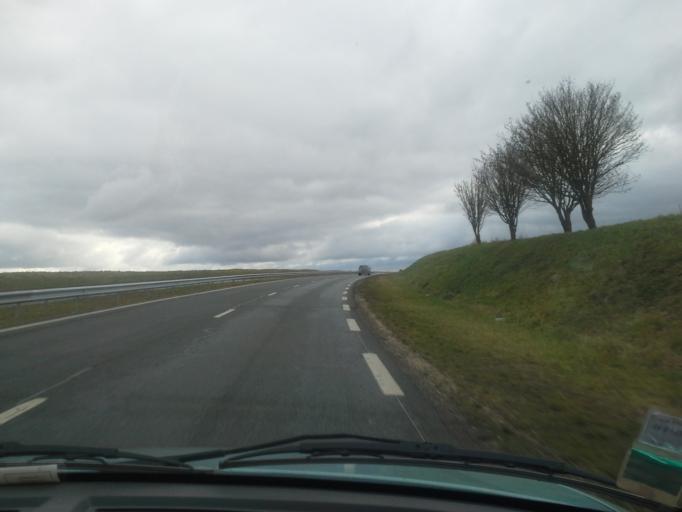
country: FR
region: Centre
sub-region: Departement du Loir-et-Cher
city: Vendome
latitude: 47.7321
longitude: 1.1487
